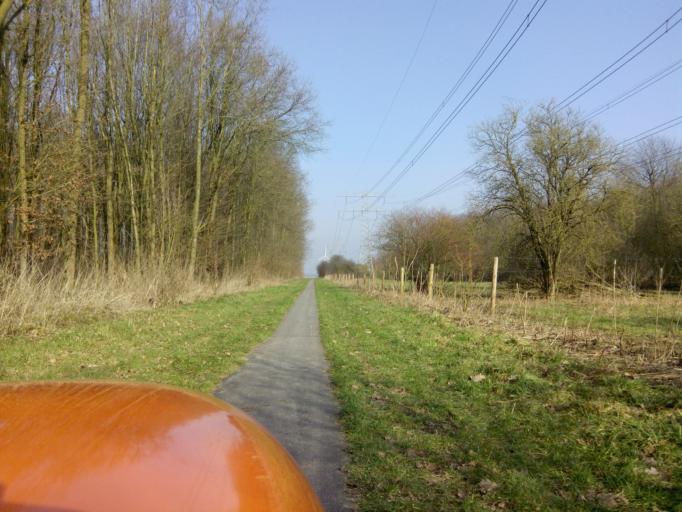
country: NL
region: Utrecht
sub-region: Gemeente Bunschoten
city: Bunschoten
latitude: 52.2736
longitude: 5.4299
